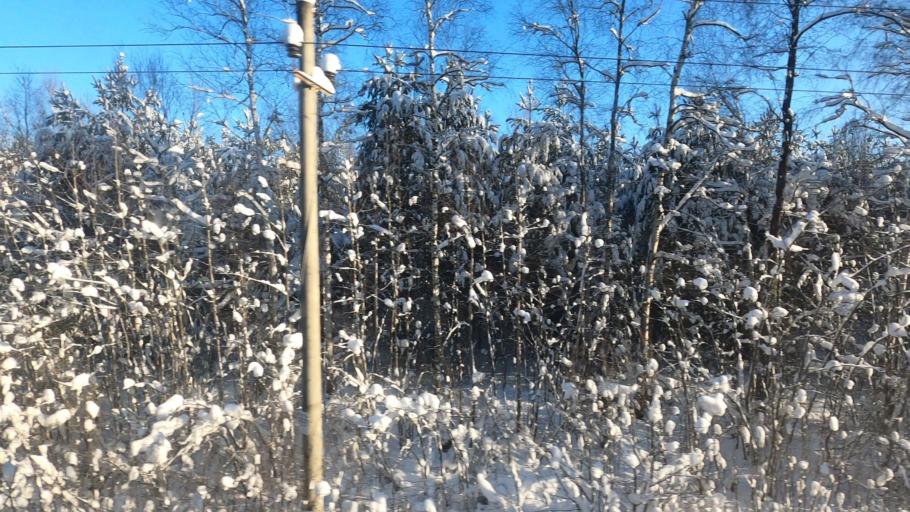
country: RU
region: Moskovskaya
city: Zhukovka
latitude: 56.4617
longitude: 37.5260
